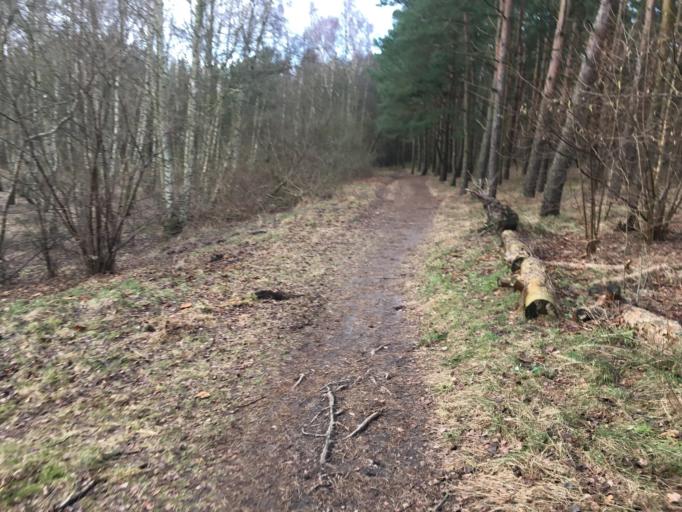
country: SE
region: Skane
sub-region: Lomma Kommun
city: Lomma
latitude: 55.6903
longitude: 13.0663
